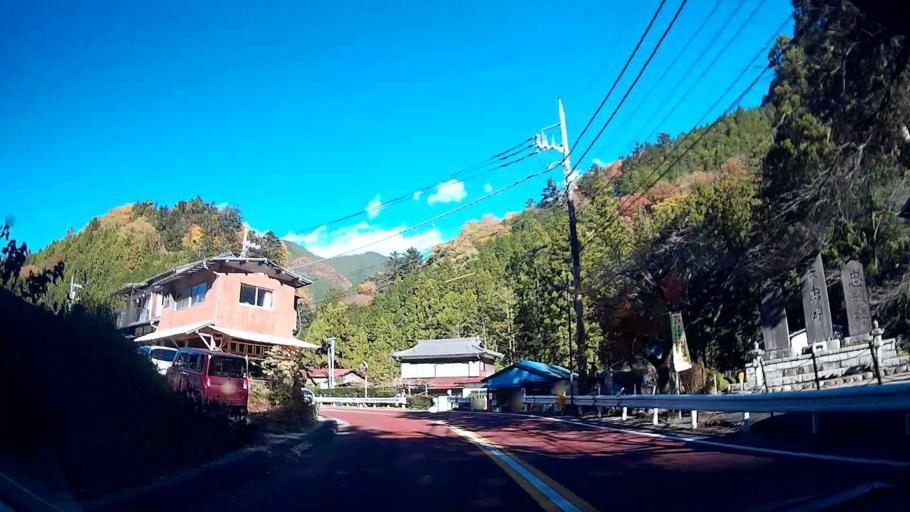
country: JP
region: Tokyo
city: Itsukaichi
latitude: 35.7231
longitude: 139.1634
